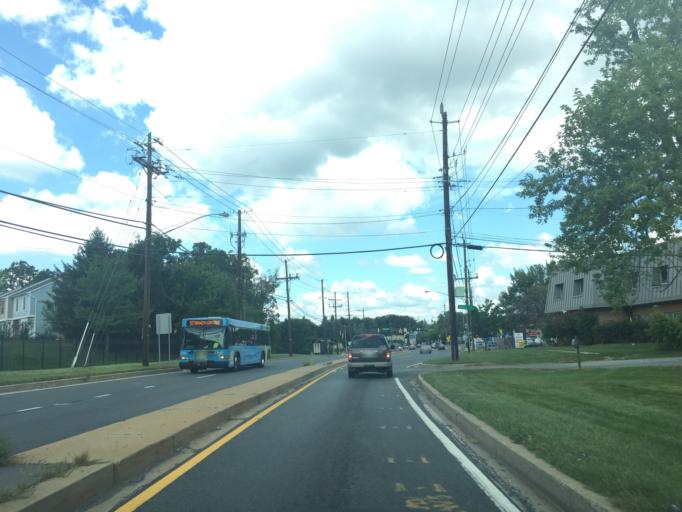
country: US
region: Maryland
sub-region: Montgomery County
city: Redland
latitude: 39.1578
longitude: -77.1588
